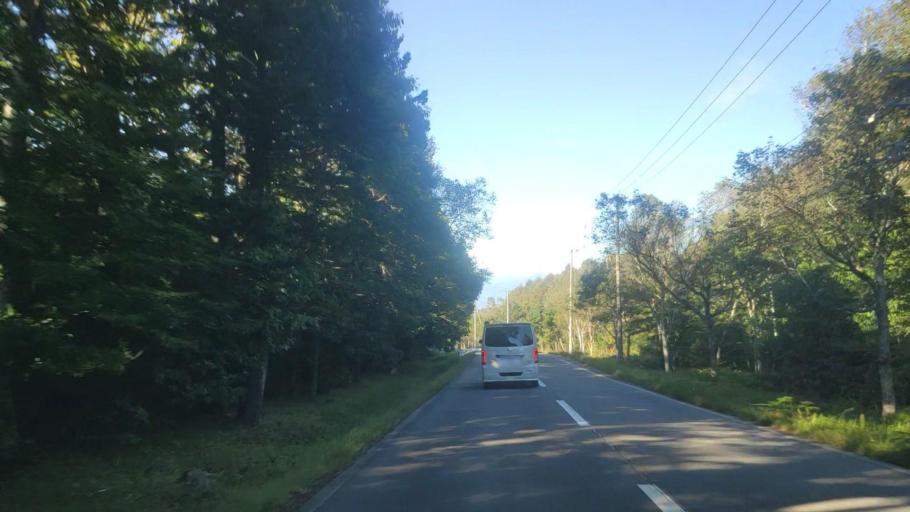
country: JP
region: Nagano
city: Kamimaruko
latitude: 36.1838
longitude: 138.2842
